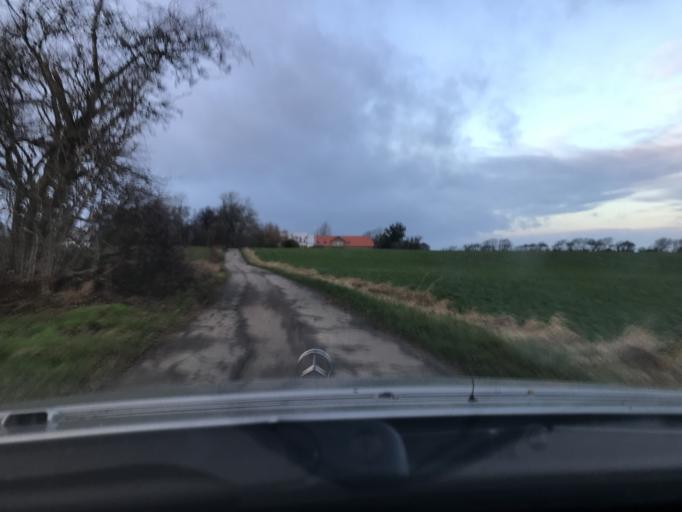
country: DK
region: South Denmark
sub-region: Sonderborg Kommune
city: Nordborg
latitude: 55.0663
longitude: 9.6932
